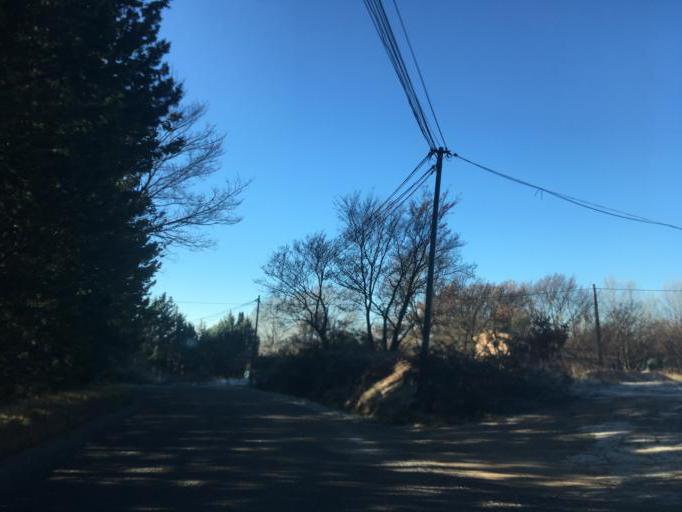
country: FR
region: Provence-Alpes-Cote d'Azur
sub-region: Departement du Var
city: Villecroze
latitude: 43.5753
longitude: 6.2735
